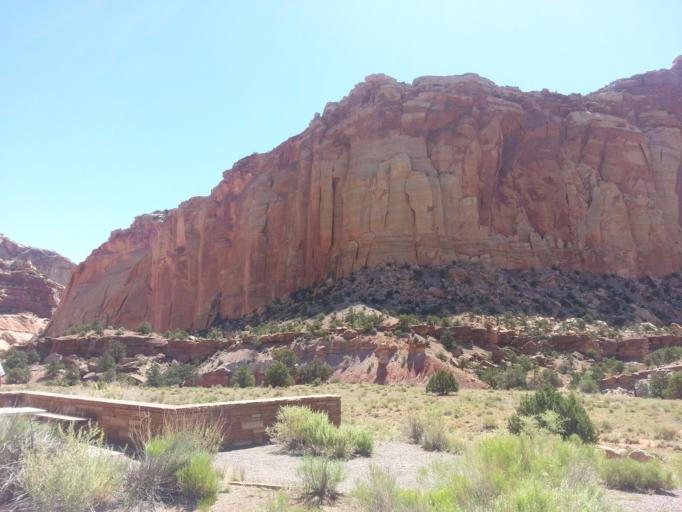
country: US
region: Utah
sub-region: Wayne County
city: Loa
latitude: 38.2083
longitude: -111.1942
